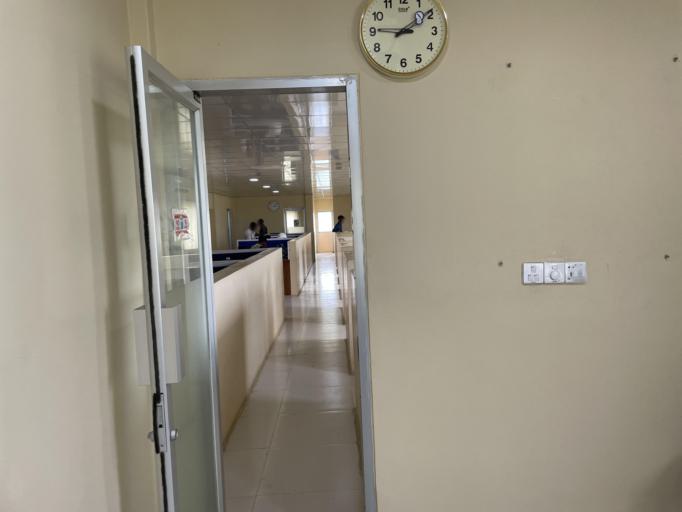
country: BD
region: Dhaka
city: Bhairab Bazar
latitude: 24.0472
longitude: 91.1096
